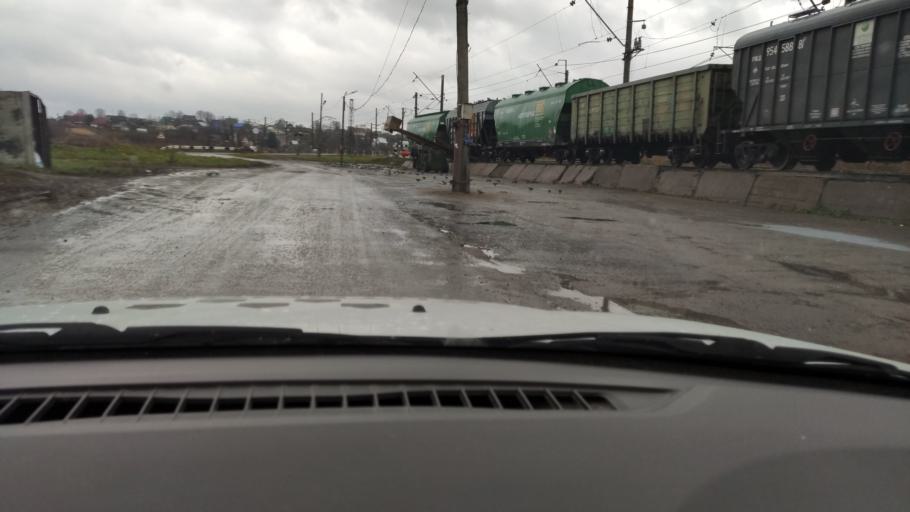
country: RU
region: Perm
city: Sylva
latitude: 58.0426
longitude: 56.7483
